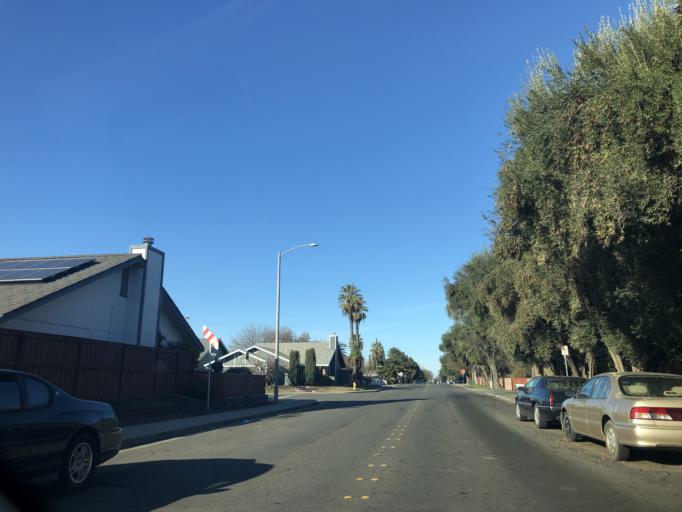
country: US
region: California
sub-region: Yolo County
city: Woodland
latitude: 38.6668
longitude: -121.7472
